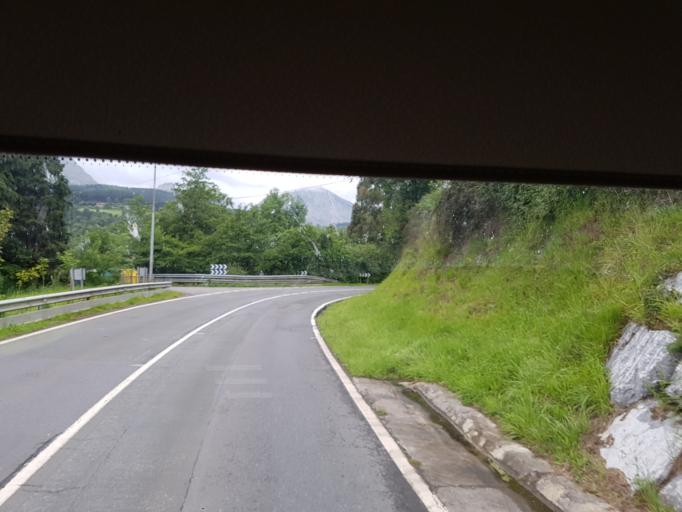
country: ES
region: Basque Country
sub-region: Bizkaia
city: Abadino
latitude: 43.1299
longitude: -2.5785
